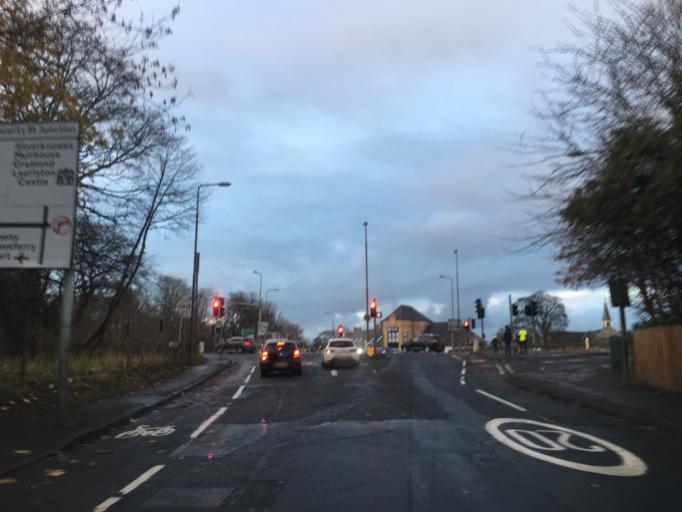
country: GB
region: Scotland
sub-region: Edinburgh
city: Colinton
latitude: 55.9621
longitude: -3.2721
